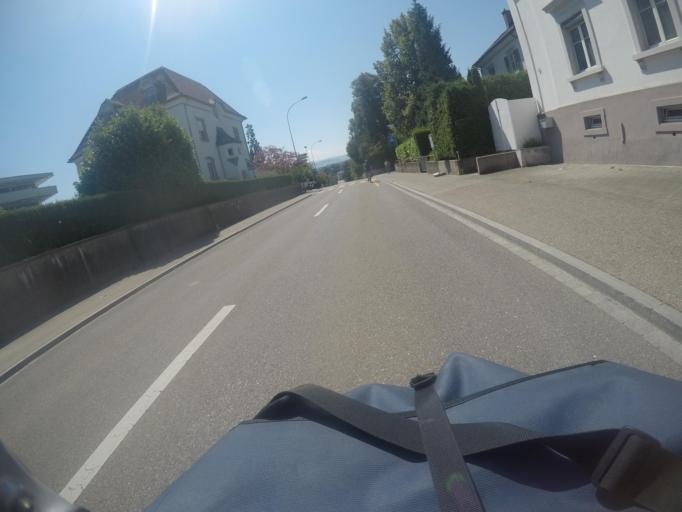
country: CH
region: Thurgau
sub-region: Arbon District
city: Arbon
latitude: 47.5149
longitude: 9.4247
